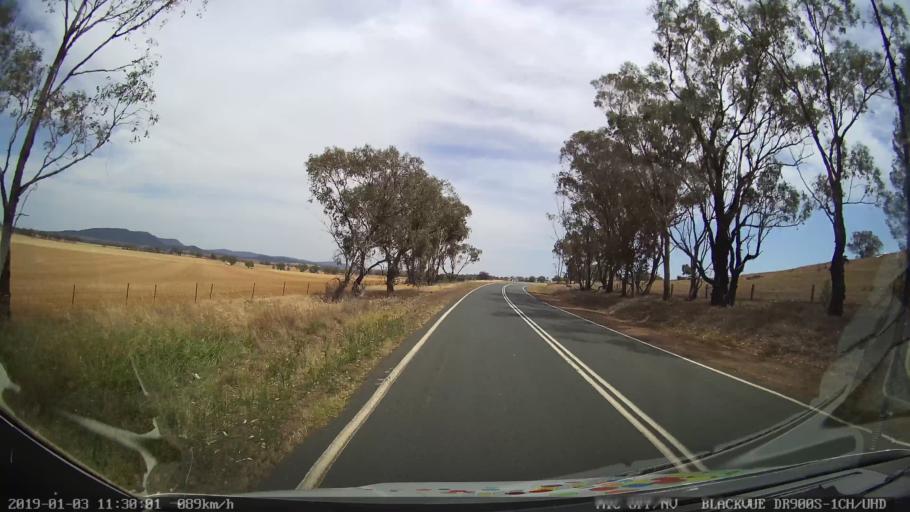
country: AU
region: New South Wales
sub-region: Weddin
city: Grenfell
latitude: -33.9875
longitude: 148.1910
